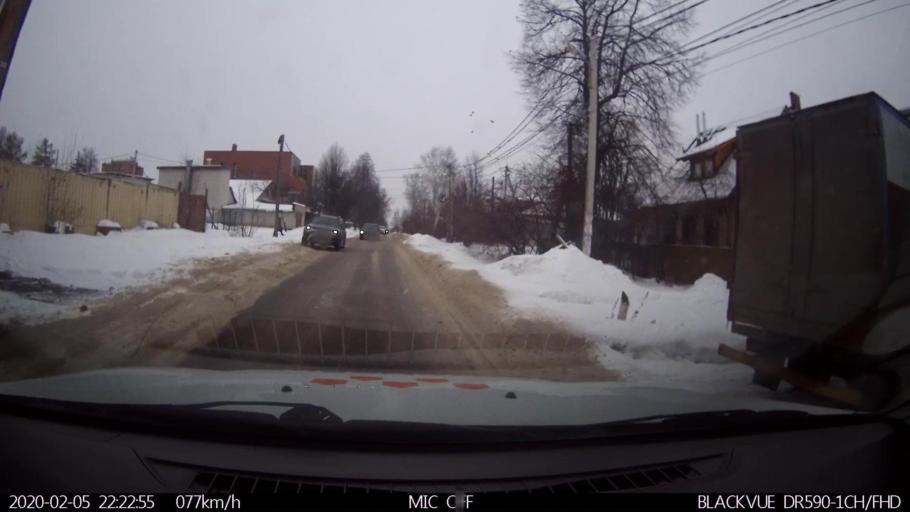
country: RU
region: Nizjnij Novgorod
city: Pervomaysk
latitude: 54.7651
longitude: 44.0208
